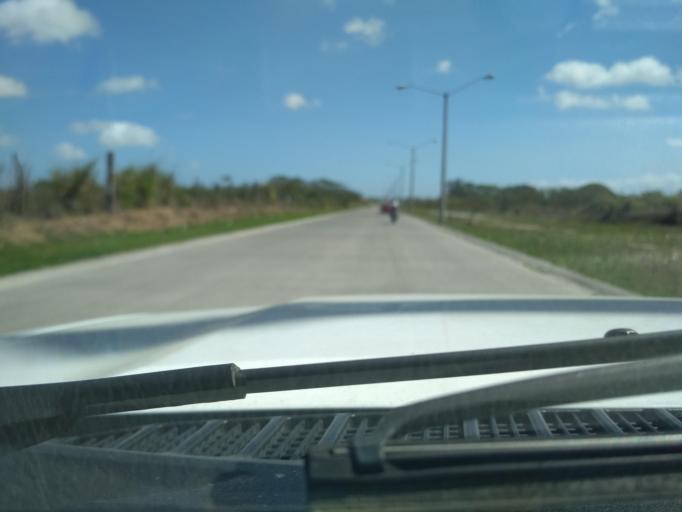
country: MX
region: Veracruz
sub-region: Veracruz
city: Las Amapolas
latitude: 19.1343
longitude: -96.2150
